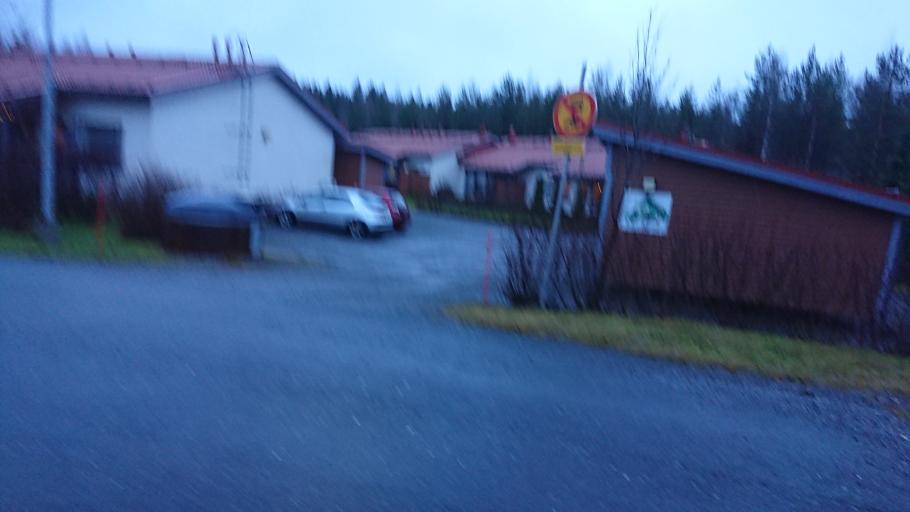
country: FI
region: Pirkanmaa
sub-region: Tampere
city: Tampere
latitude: 61.4421
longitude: 23.8736
